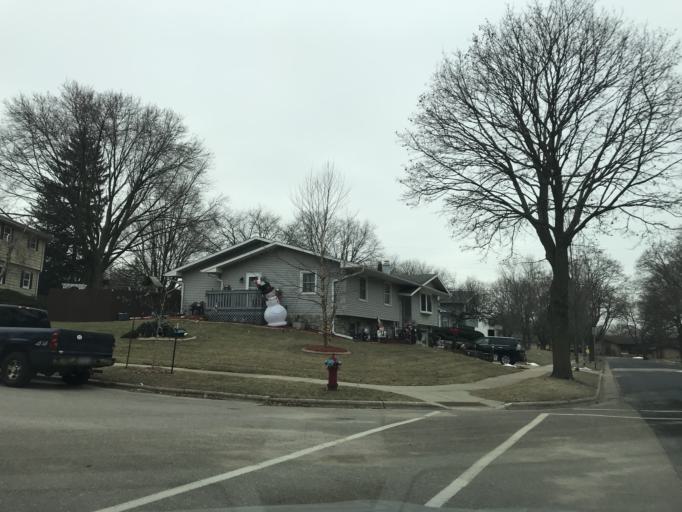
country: US
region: Wisconsin
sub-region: Dane County
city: Monona
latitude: 43.0905
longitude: -89.2920
